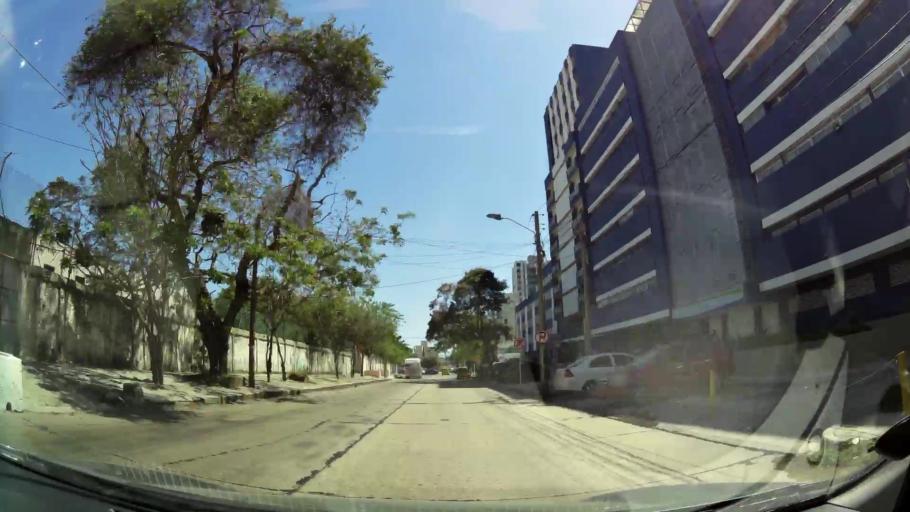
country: CO
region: Atlantico
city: Barranquilla
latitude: 10.9932
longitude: -74.8123
